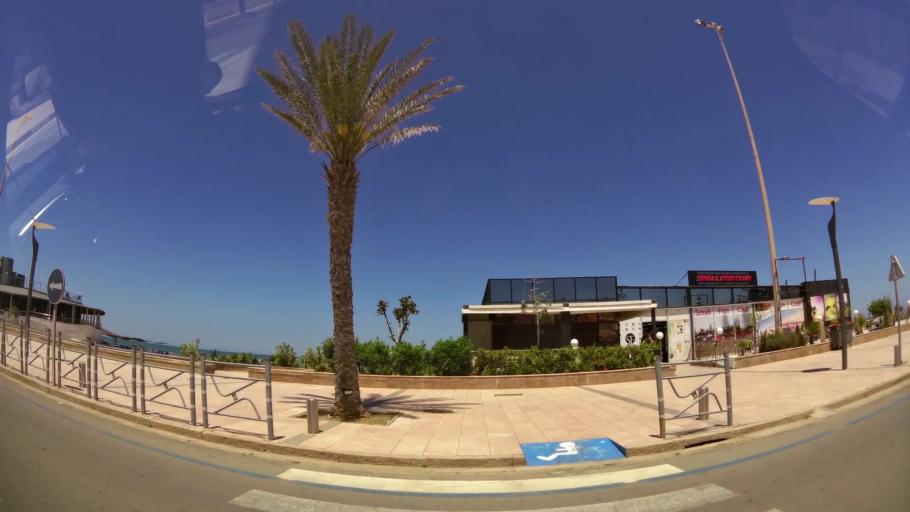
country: MA
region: Oriental
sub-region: Berkane-Taourirt
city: Madagh
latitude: 35.0875
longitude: -2.2296
